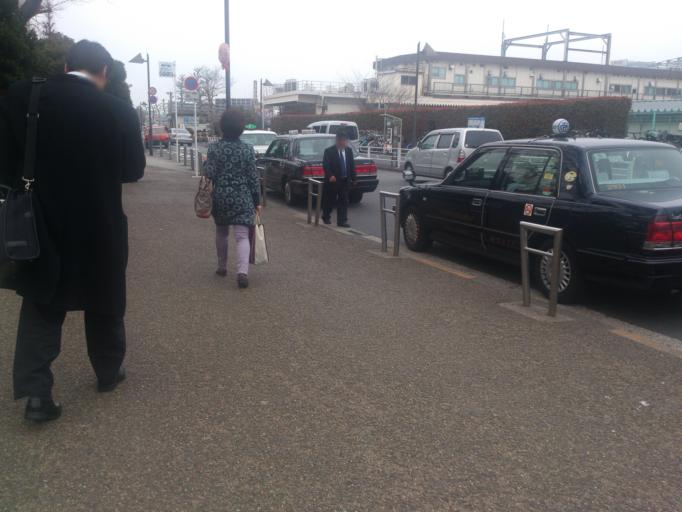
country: JP
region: Tokyo
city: Tokyo
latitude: 35.7140
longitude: 139.7759
